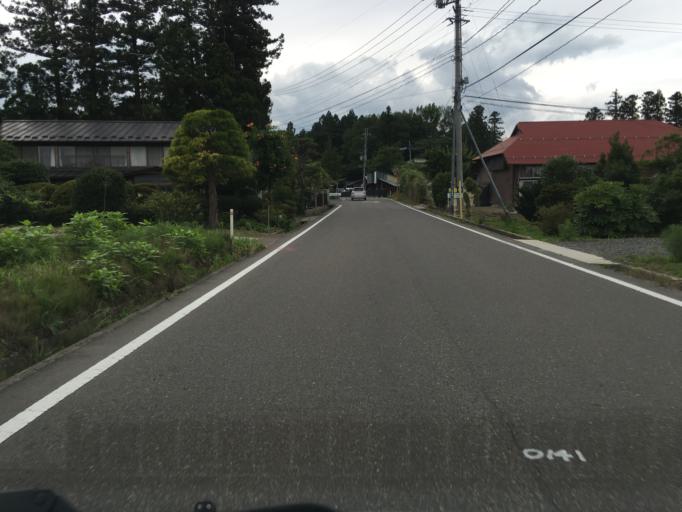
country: JP
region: Fukushima
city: Fukushima-shi
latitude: 37.7794
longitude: 140.4165
